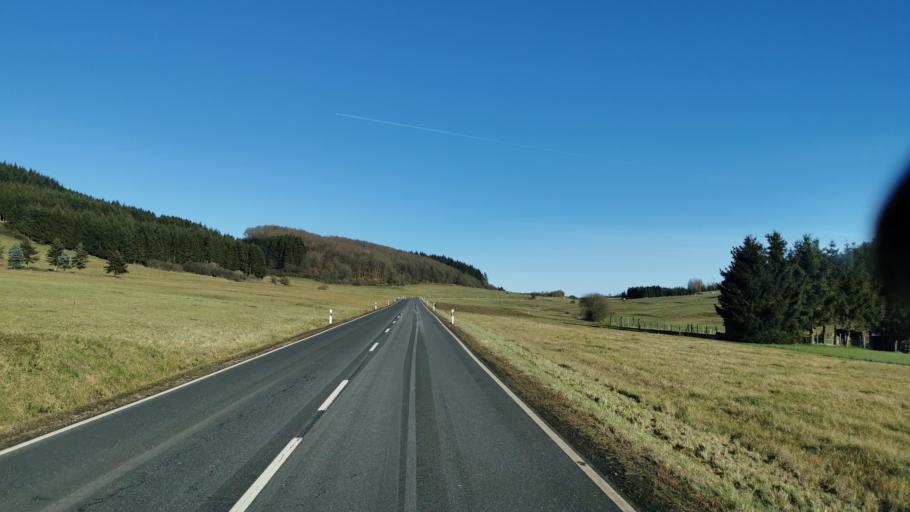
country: DE
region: Rheinland-Pfalz
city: Oberstadtfeld
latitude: 50.1784
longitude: 6.7745
